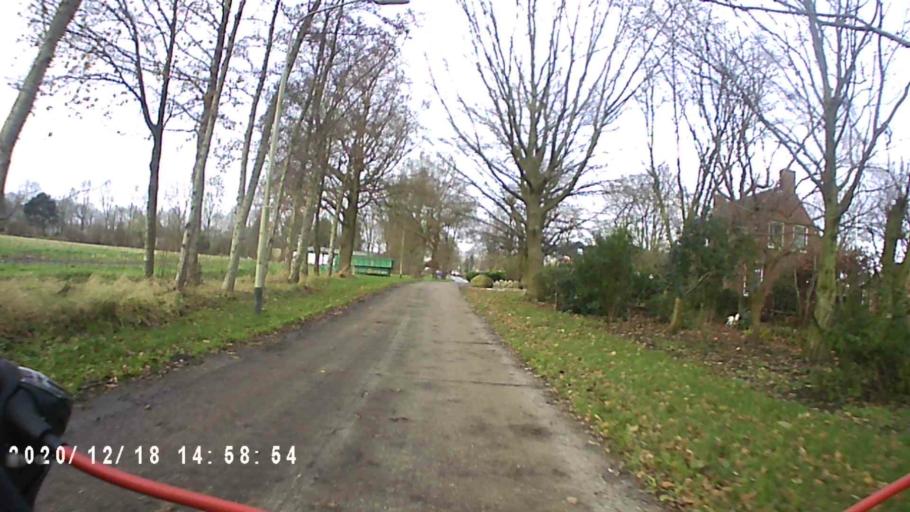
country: NL
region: Groningen
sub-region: Gemeente Hoogezand-Sappemeer
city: Hoogezand
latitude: 53.1792
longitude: 6.6905
